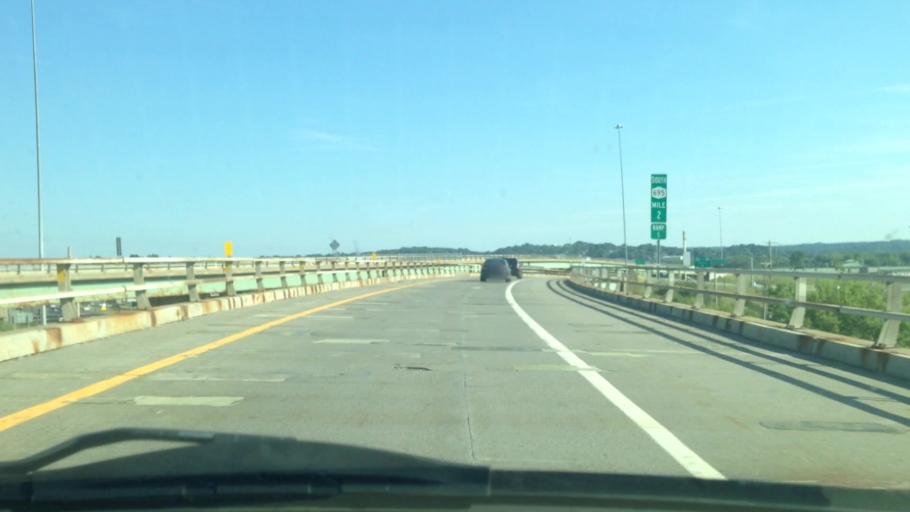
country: US
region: New York
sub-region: Onondaga County
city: Lakeland
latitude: 43.0818
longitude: -76.2265
